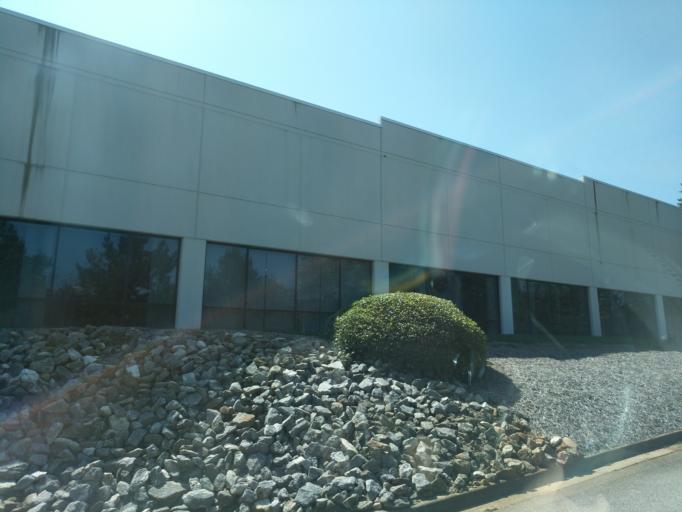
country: US
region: South Carolina
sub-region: Spartanburg County
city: Valley Falls
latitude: 35.0029
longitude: -81.9357
